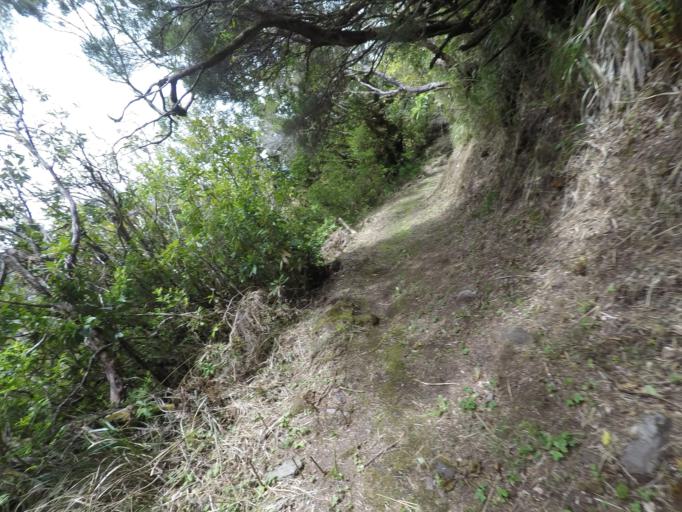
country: PT
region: Madeira
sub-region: Camara de Lobos
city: Curral das Freiras
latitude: 32.7666
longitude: -16.9754
